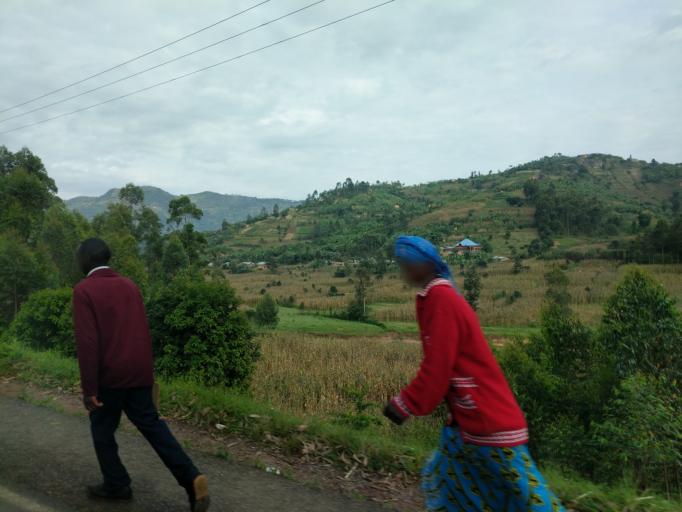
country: RW
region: Northern Province
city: Musanze
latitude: -1.6486
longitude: 29.8007
